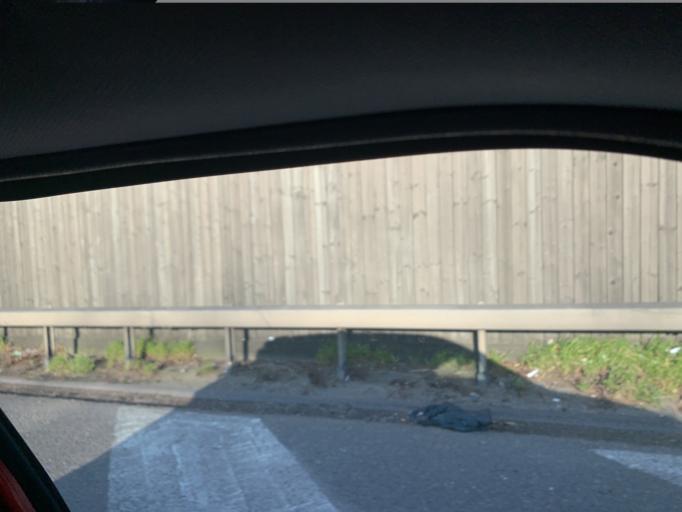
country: GB
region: England
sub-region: Surrey
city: Leatherhead
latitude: 51.3045
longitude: -0.3211
